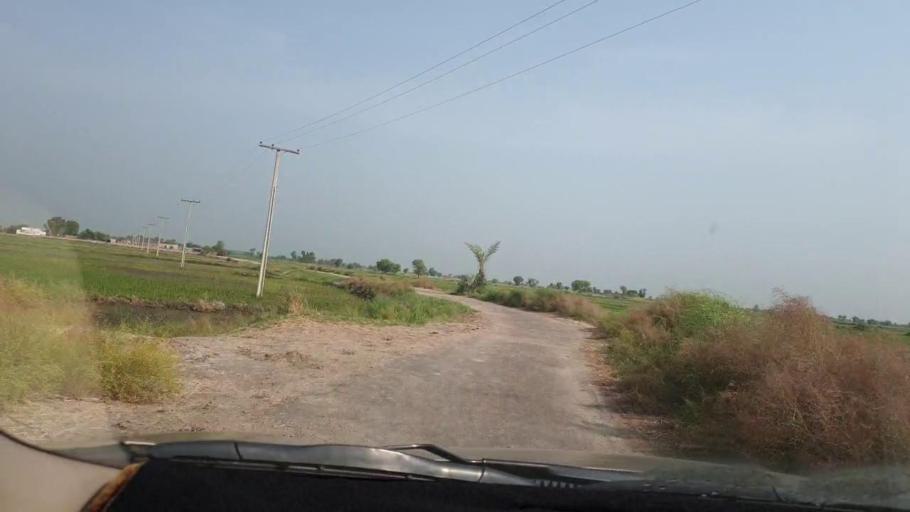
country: PK
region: Sindh
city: Goth Garelo
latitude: 27.4617
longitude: 68.0517
